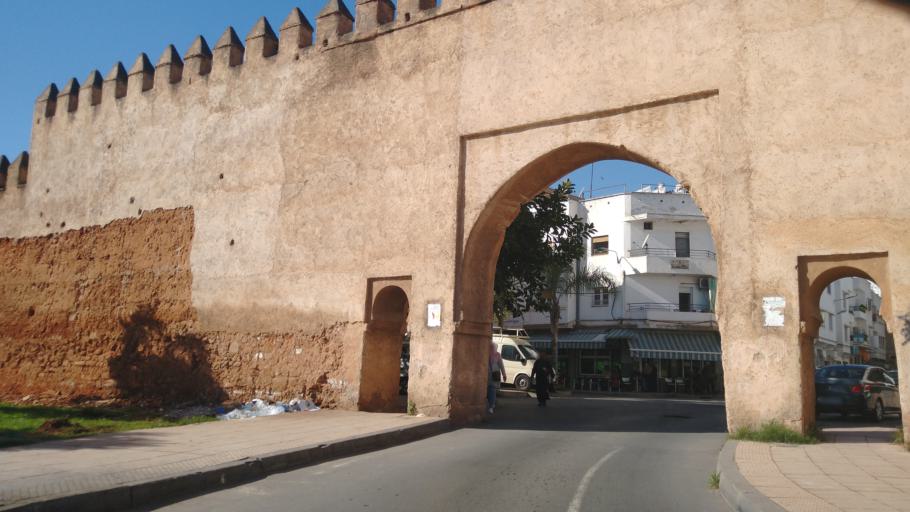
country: MA
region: Rabat-Sale-Zemmour-Zaer
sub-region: Rabat
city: Rabat
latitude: 34.0344
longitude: -6.8193
